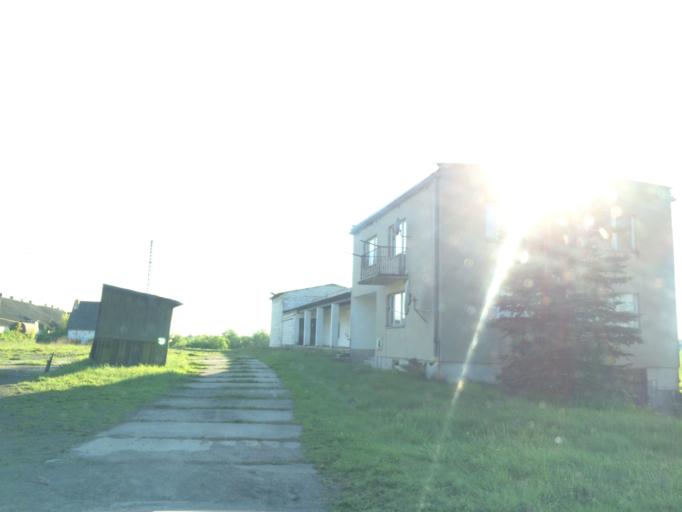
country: PL
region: Warmian-Masurian Voivodeship
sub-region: Powiat dzialdowski
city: Lidzbark
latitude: 53.2710
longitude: 19.7699
